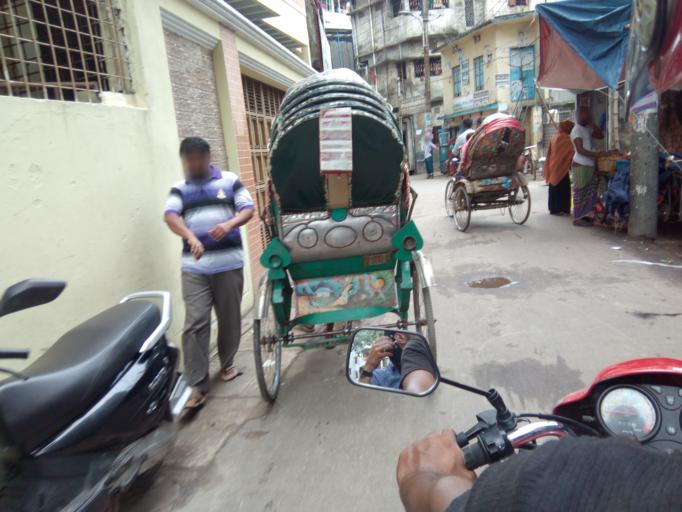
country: BD
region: Dhaka
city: Azimpur
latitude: 23.7309
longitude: 90.3714
